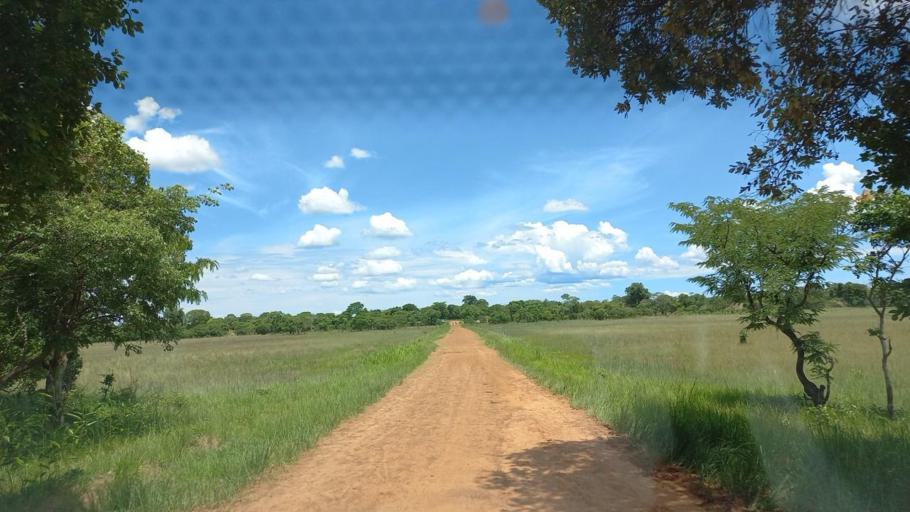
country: ZM
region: North-Western
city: Kabompo
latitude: -12.7504
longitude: 24.2679
